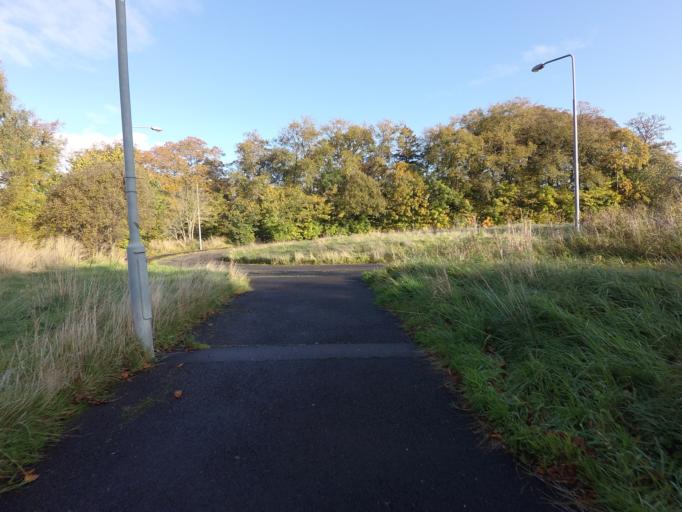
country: GB
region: Scotland
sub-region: West Lothian
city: West Calder
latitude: 55.8629
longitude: -3.5419
